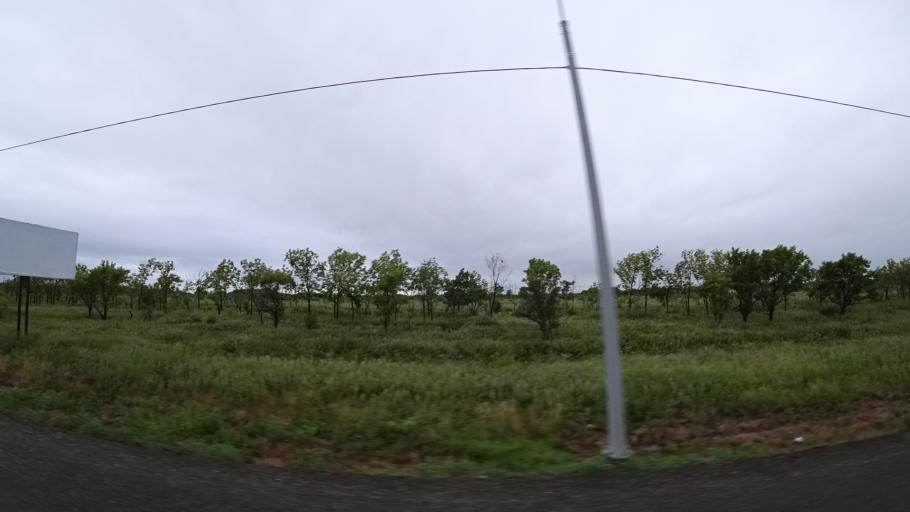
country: RU
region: Primorskiy
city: Chernigovka
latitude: 44.3258
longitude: 132.5713
